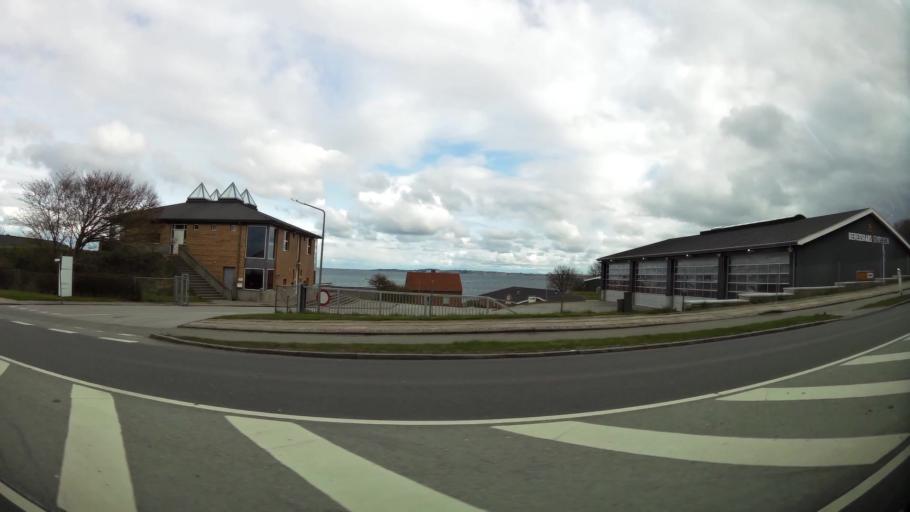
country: DK
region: North Denmark
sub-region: Thisted Kommune
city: Thisted
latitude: 56.9489
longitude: 8.6632
